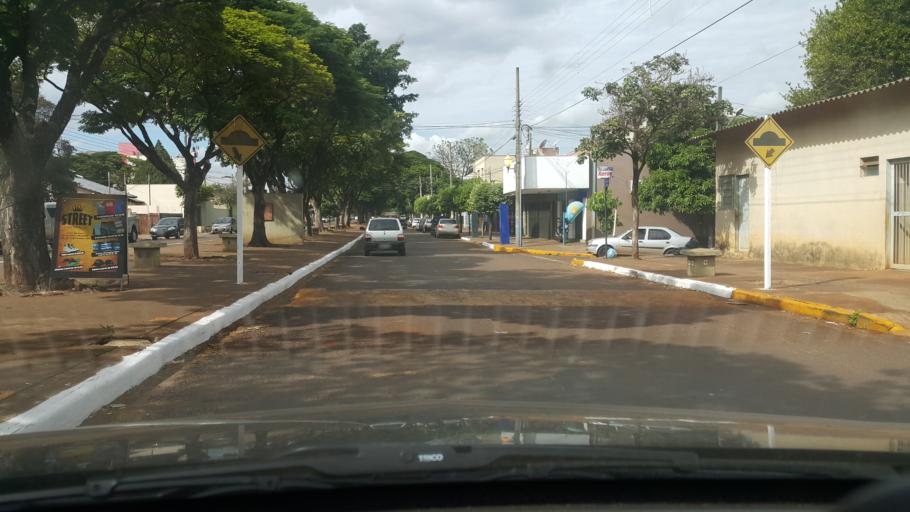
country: BR
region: Mato Grosso do Sul
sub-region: Dourados
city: Dourados
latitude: -22.2329
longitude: -54.8136
